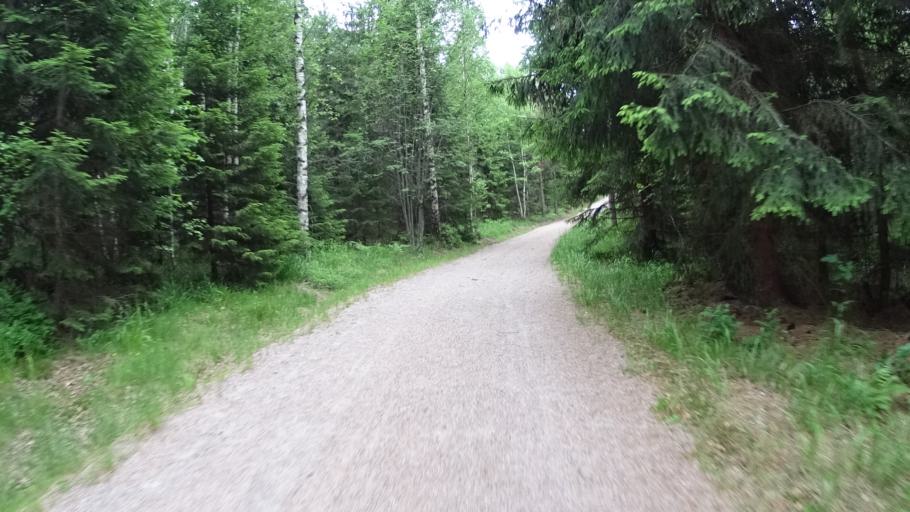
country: FI
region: Uusimaa
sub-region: Helsinki
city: Espoo
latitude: 60.2763
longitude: 24.6181
